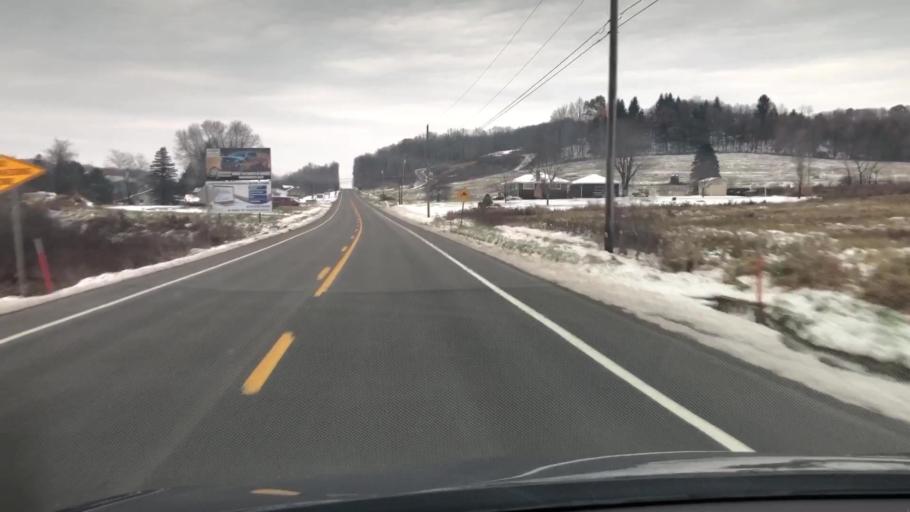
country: US
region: Pennsylvania
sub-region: Jefferson County
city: Brookville
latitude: 41.0679
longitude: -79.2402
